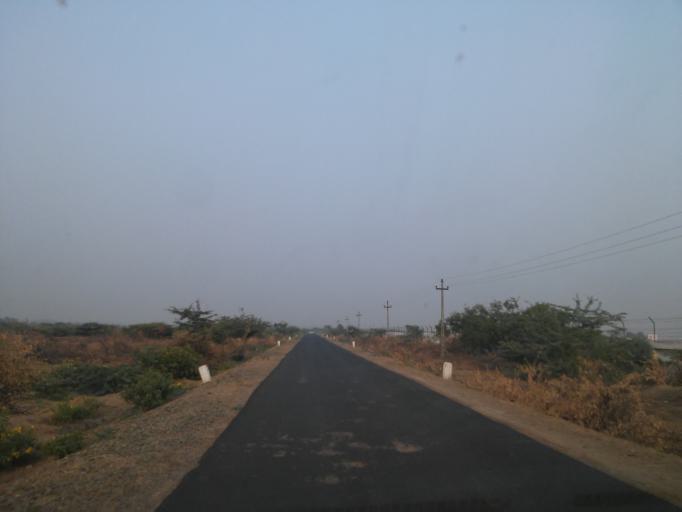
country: IN
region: Gujarat
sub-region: Kachchh
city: Mandvi
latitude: 22.8397
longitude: 69.2982
